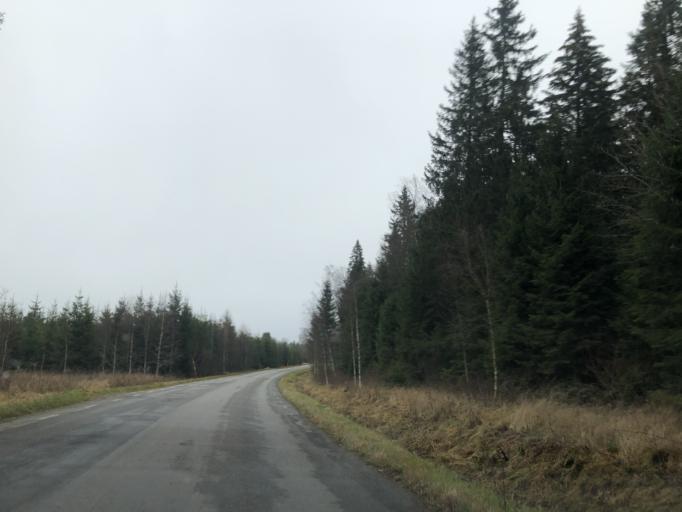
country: SE
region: Vaestra Goetaland
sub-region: Ulricehamns Kommun
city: Ulricehamn
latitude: 57.6916
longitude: 13.4807
